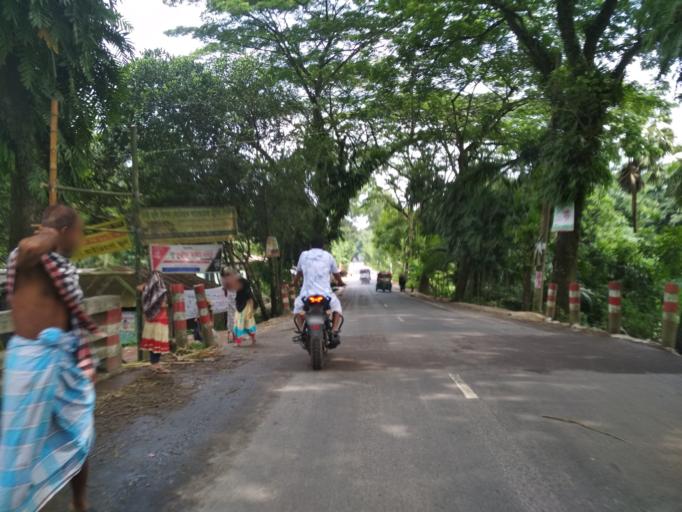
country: BD
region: Chittagong
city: Lakshmipur
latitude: 22.9527
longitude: 90.8089
